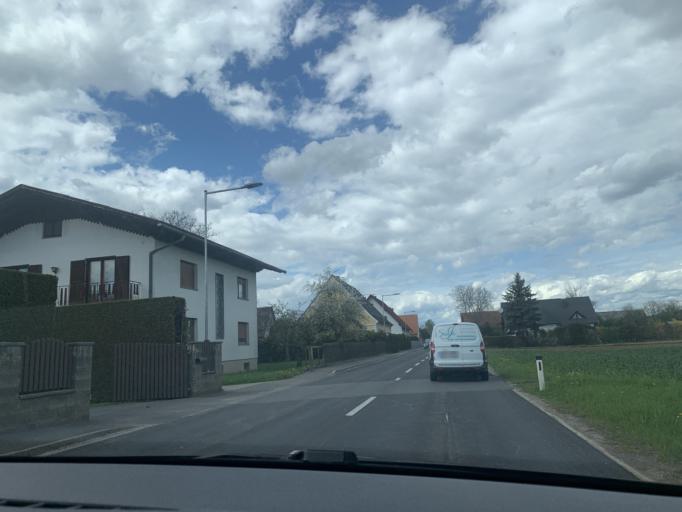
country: AT
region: Styria
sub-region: Politischer Bezirk Graz-Umgebung
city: Zettling
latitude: 46.9208
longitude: 15.3998
